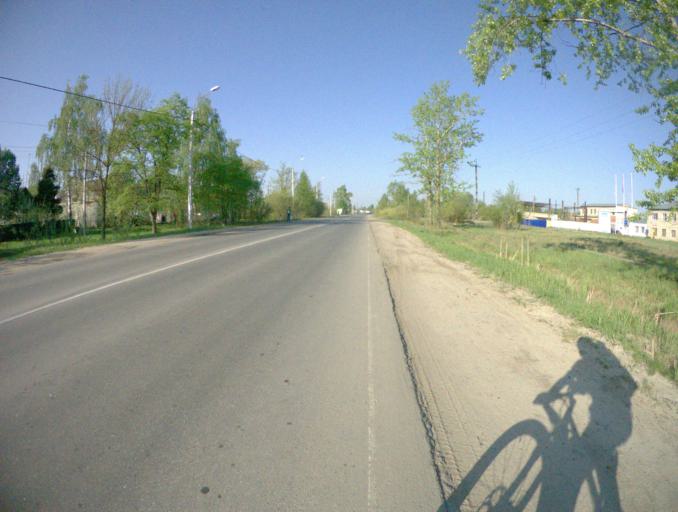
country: RU
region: Vladimir
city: Novovyazniki
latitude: 56.2100
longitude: 42.1669
